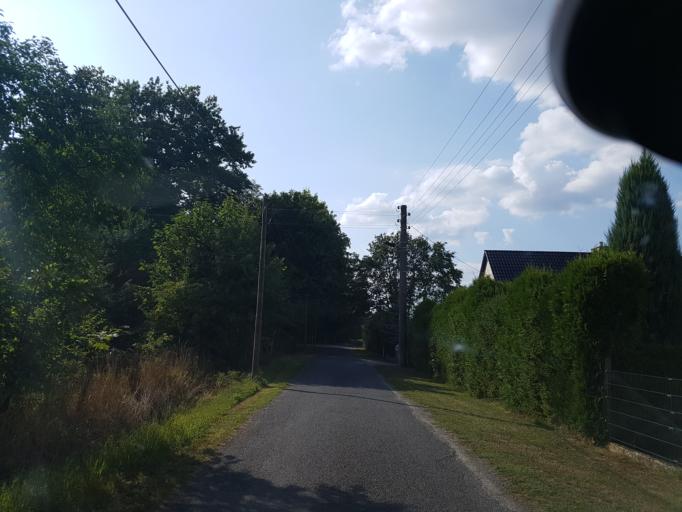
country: DE
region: Brandenburg
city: Calau
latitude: 51.7746
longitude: 13.9547
